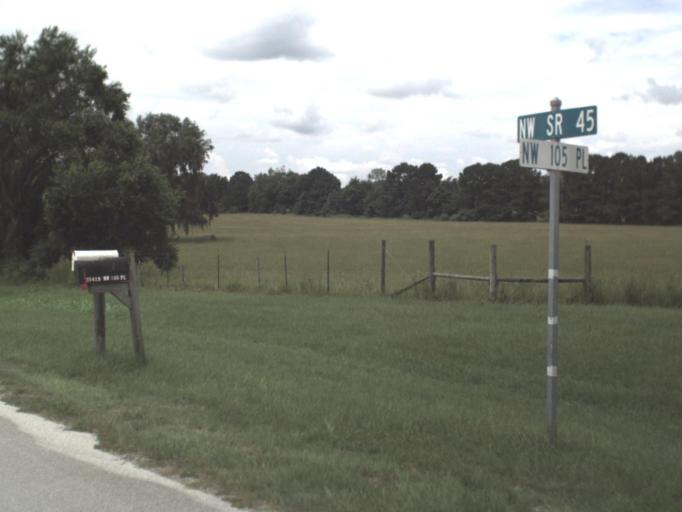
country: US
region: Florida
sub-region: Alachua County
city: High Springs
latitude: 29.7537
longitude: -82.6074
